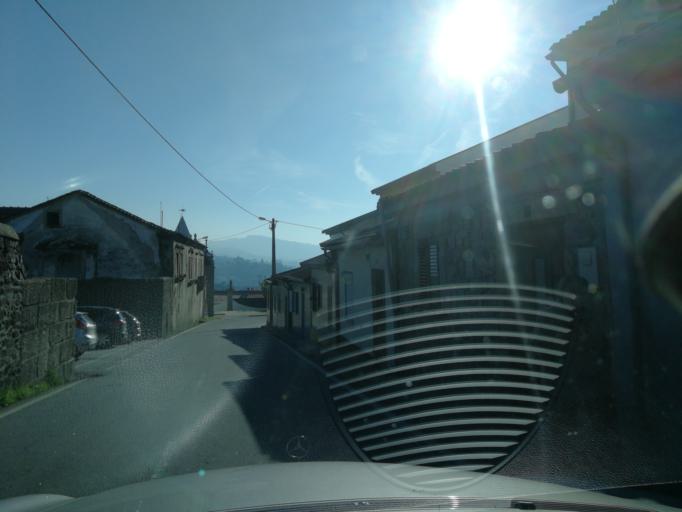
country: PT
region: Braga
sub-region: Braga
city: Adaufe
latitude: 41.5696
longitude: -8.3891
